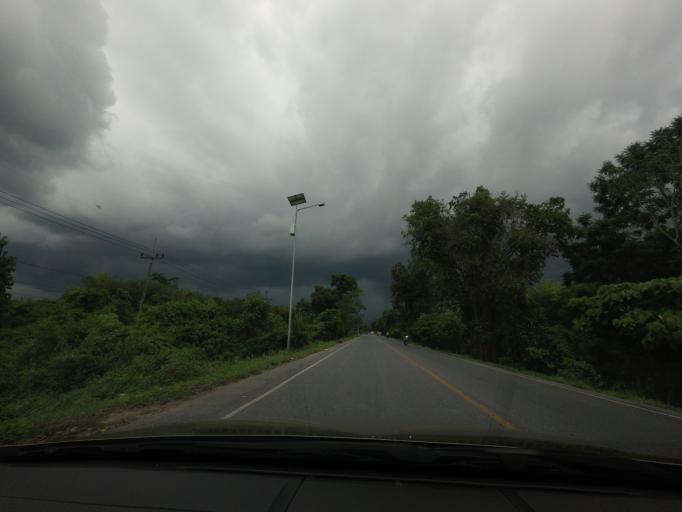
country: TH
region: Narathiwat
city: Rueso
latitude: 6.3504
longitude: 101.4922
